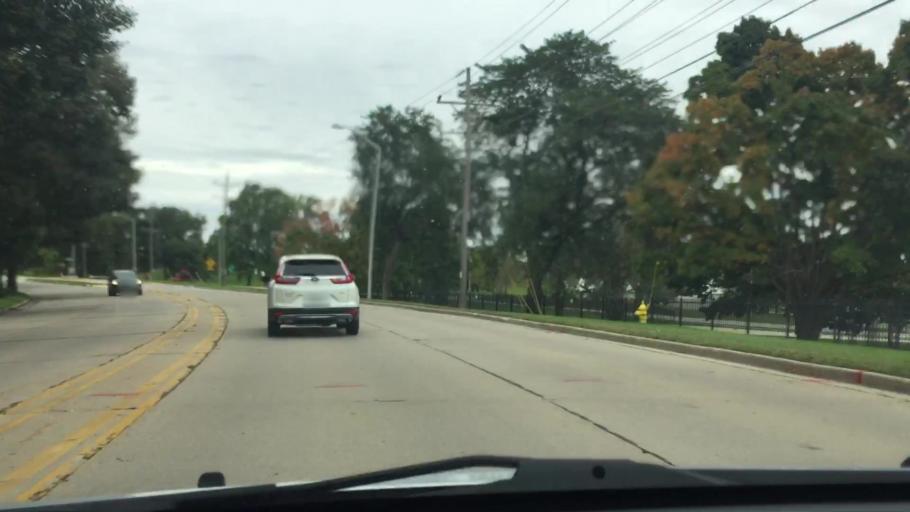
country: US
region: Wisconsin
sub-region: Waukesha County
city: Waukesha
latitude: 43.0312
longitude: -88.2437
